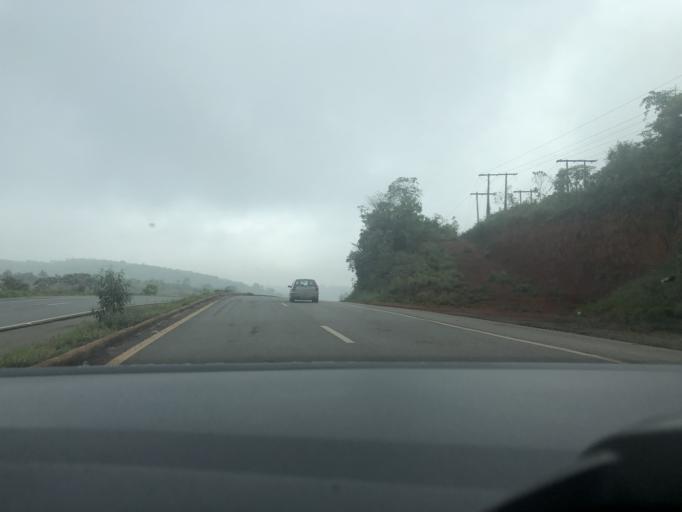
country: BR
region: Minas Gerais
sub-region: Congonhas
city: Congonhas
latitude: -20.5878
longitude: -43.9449
